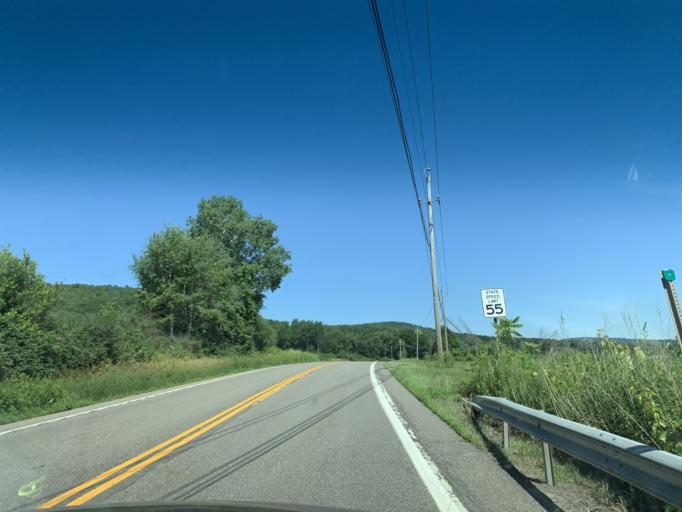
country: US
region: New York
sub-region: Chenango County
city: Norwich
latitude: 42.5018
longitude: -75.4032
